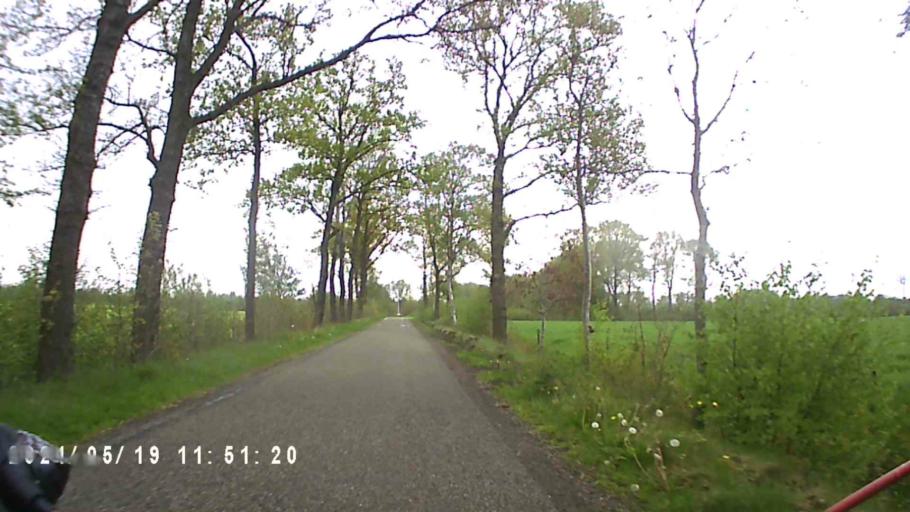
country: NL
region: Friesland
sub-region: Gemeente Kollumerland en Nieuwkruisland
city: Kollum
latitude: 53.2694
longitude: 6.1423
